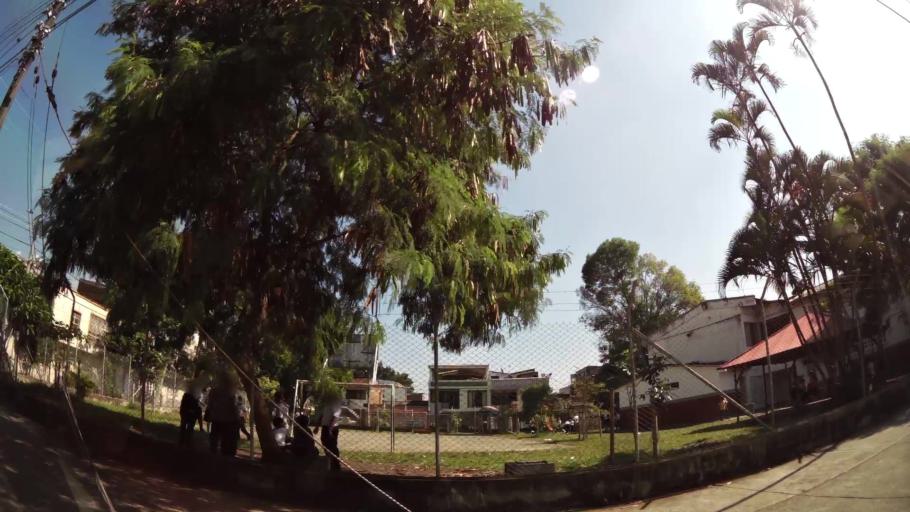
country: CO
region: Valle del Cauca
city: Cali
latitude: 3.4215
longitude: -76.5290
